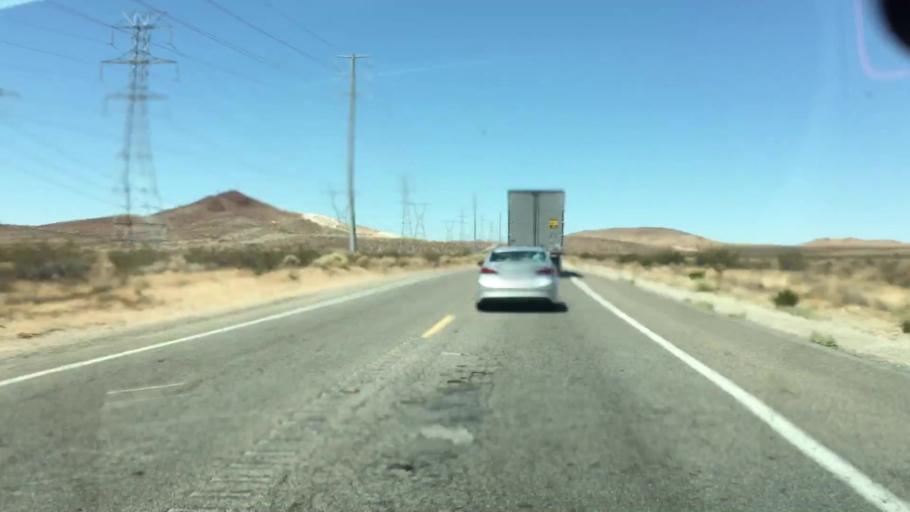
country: US
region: California
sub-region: Kern County
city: Boron
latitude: 34.8557
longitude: -117.5037
